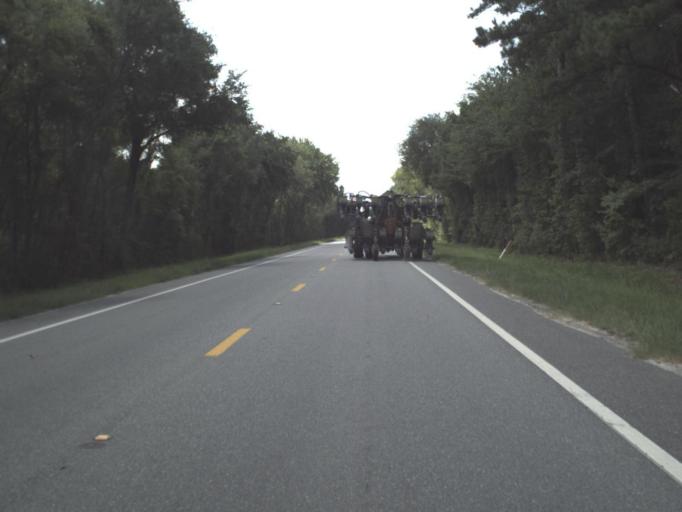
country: US
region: Georgia
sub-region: Echols County
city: Statenville
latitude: 30.5743
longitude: -83.0817
